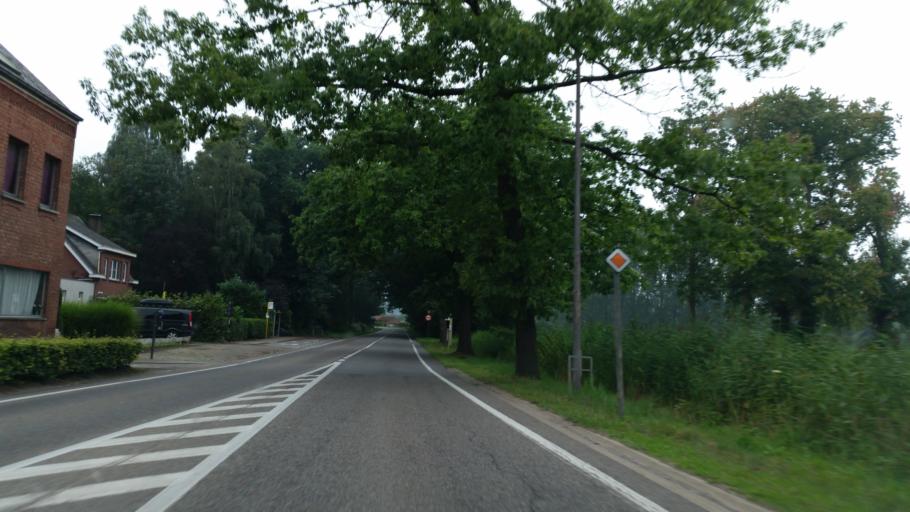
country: BE
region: Flanders
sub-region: Provincie Antwerpen
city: Hoogstraten
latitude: 51.4017
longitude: 4.7763
